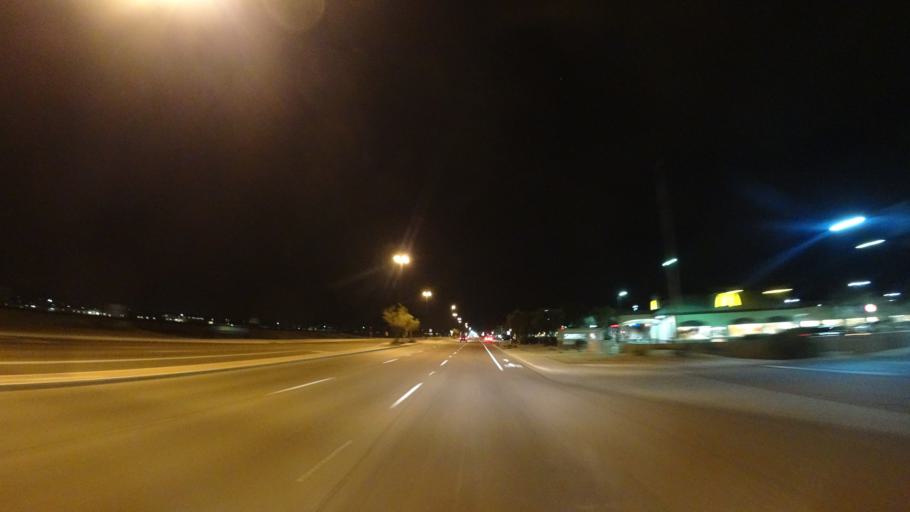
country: US
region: Arizona
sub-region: Maricopa County
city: Gilbert
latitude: 33.3788
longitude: -111.7225
